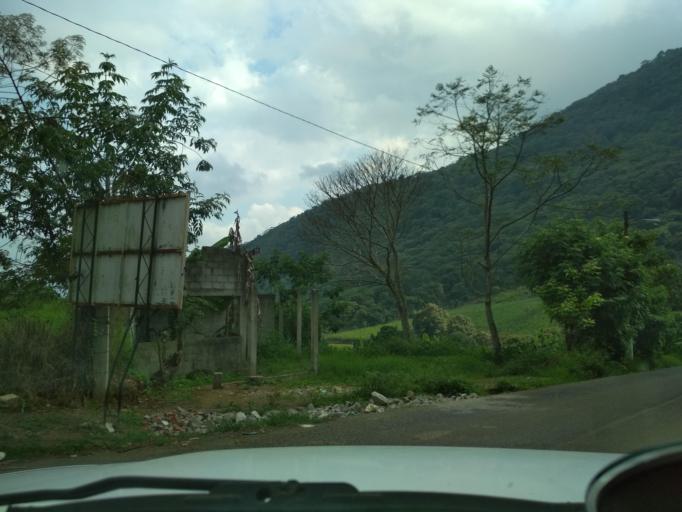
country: MX
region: Veracruz
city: Tocuila
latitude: 18.9469
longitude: -97.0314
